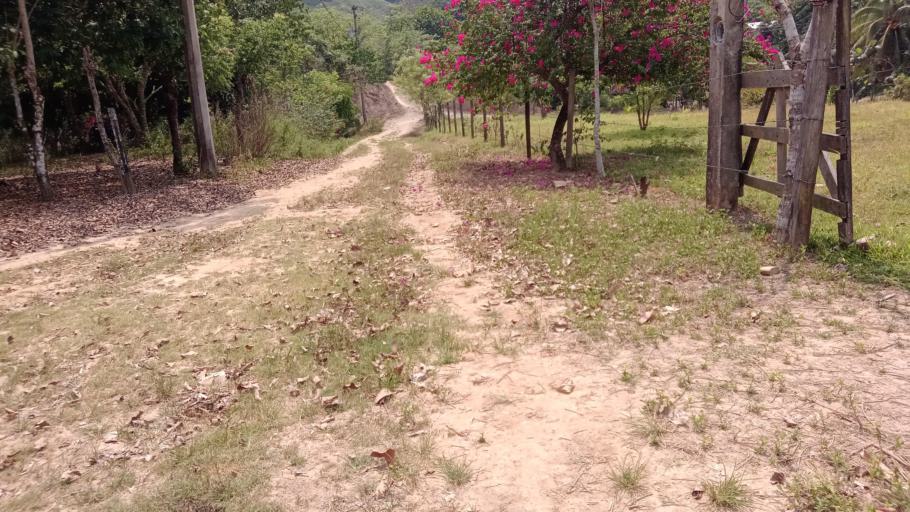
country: MX
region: Tabasco
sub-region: Huimanguillo
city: Francisco Rueda
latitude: 17.5893
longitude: -93.8560
